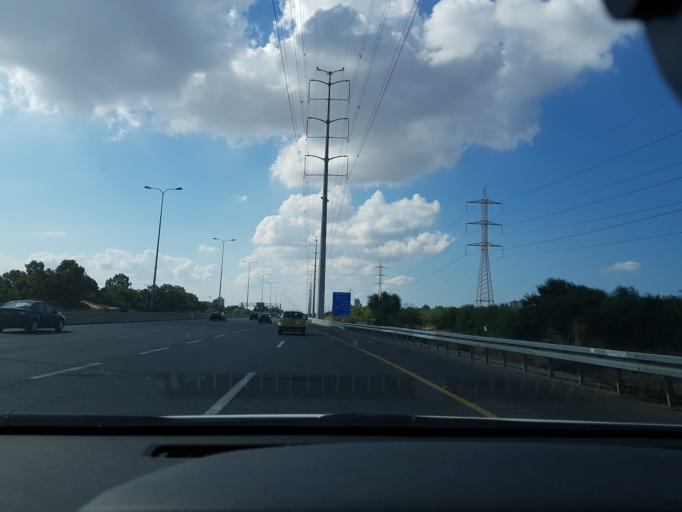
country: IL
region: Central District
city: Bet Dagan
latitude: 31.9950
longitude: 34.7996
